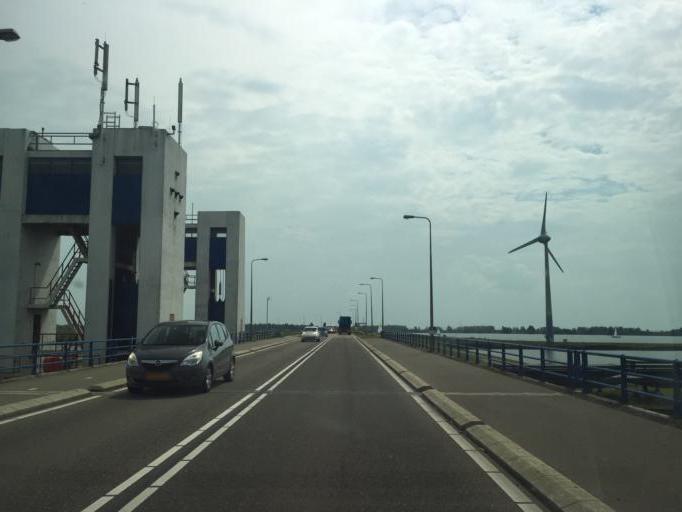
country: NL
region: North Holland
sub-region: Gemeente Enkhuizen
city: Enkhuizen
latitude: 52.6923
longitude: 5.2834
